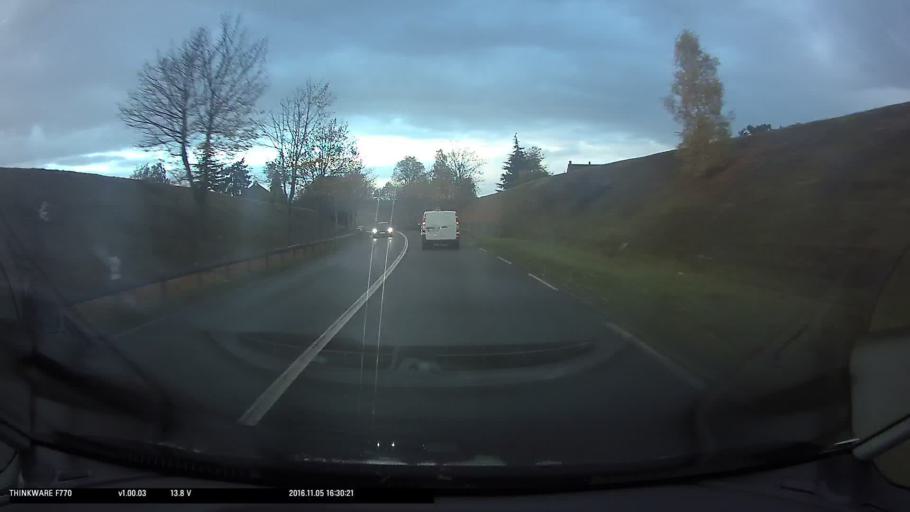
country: FR
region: Ile-de-France
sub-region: Departement du Val-d'Oise
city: Sagy
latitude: 49.0438
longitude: 1.9537
